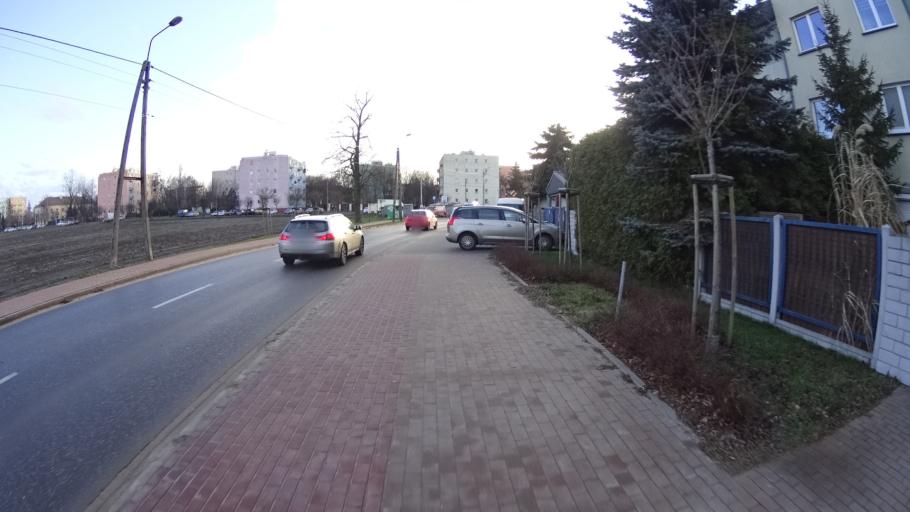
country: PL
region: Masovian Voivodeship
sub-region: Powiat warszawski zachodni
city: Ozarow Mazowiecki
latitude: 52.2138
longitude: 20.7992
